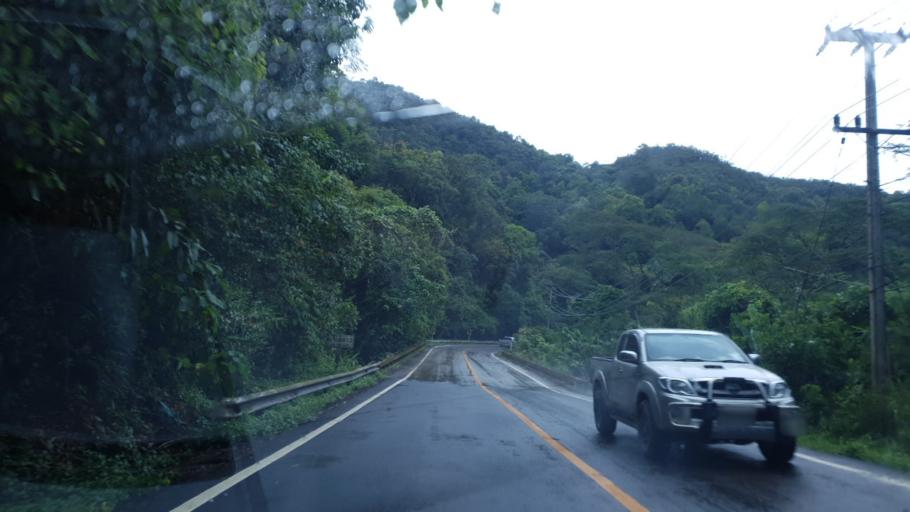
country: TH
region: Mae Hong Son
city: Ban Huai I Huak
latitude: 18.1403
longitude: 98.0856
